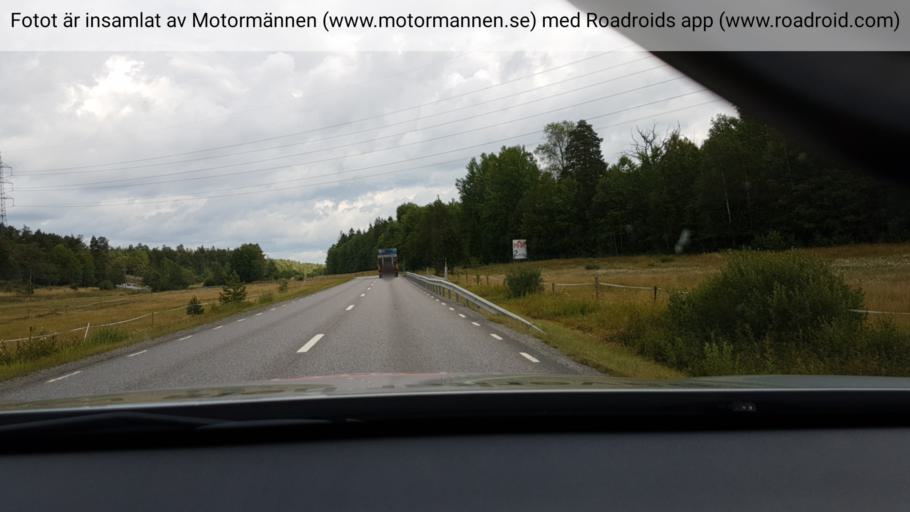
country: SE
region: Stockholm
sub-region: Haninge Kommun
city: Jordbro
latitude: 59.1848
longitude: 18.0972
